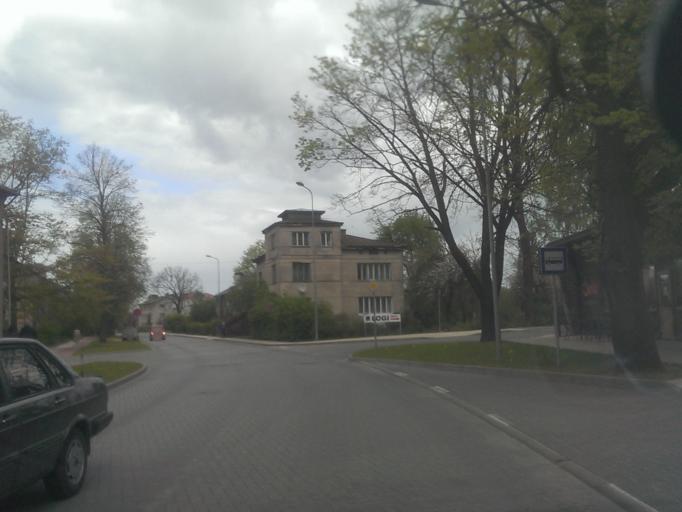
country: LV
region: Kuldigas Rajons
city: Kuldiga
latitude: 56.9697
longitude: 21.9602
